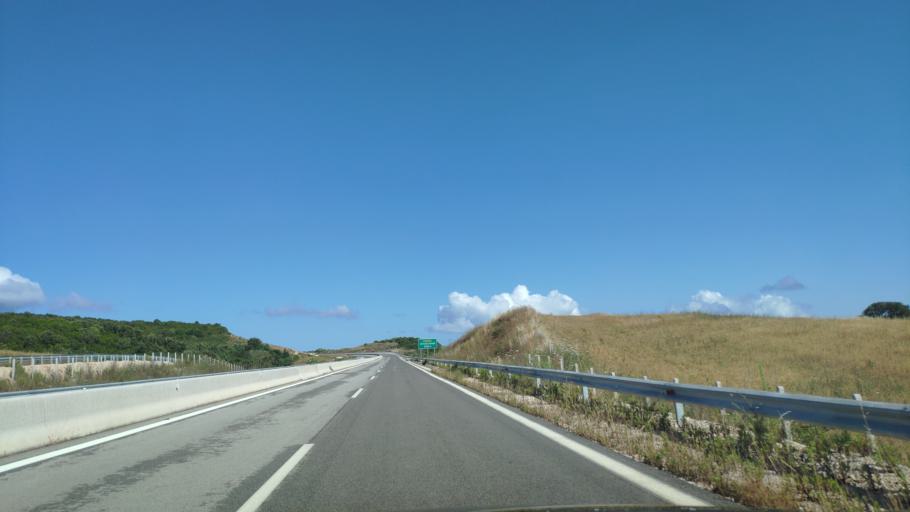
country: GR
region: West Greece
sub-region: Nomos Aitolias kai Akarnanias
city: Vonitsa
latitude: 38.9121
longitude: 20.8295
